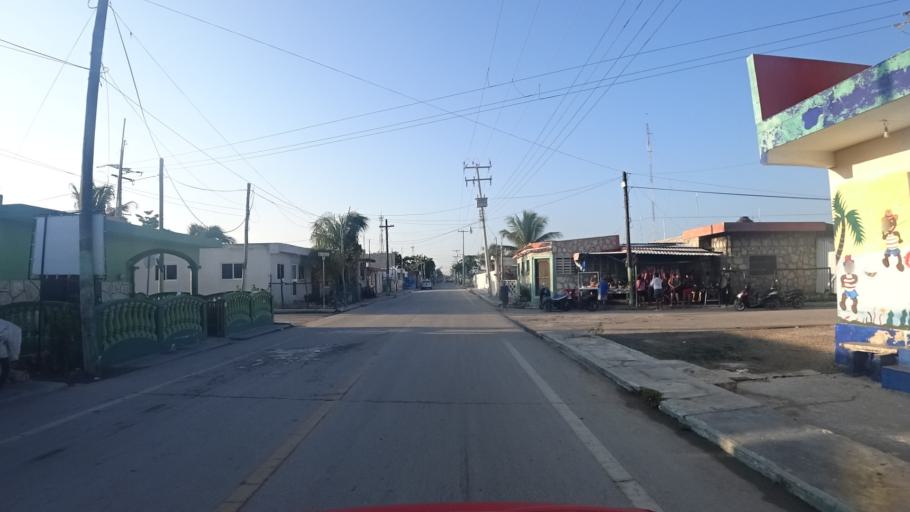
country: MX
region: Yucatan
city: Rio Lagartos
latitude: 21.5947
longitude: -88.1577
